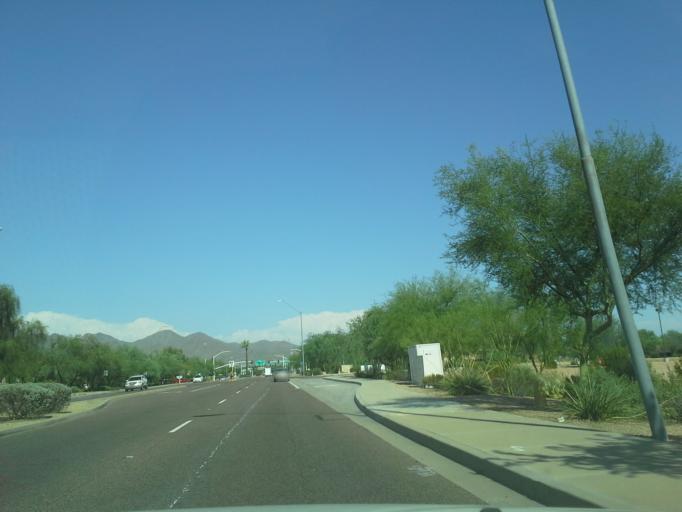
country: US
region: Arizona
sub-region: Maricopa County
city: Paradise Valley
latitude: 33.6183
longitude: -111.8963
